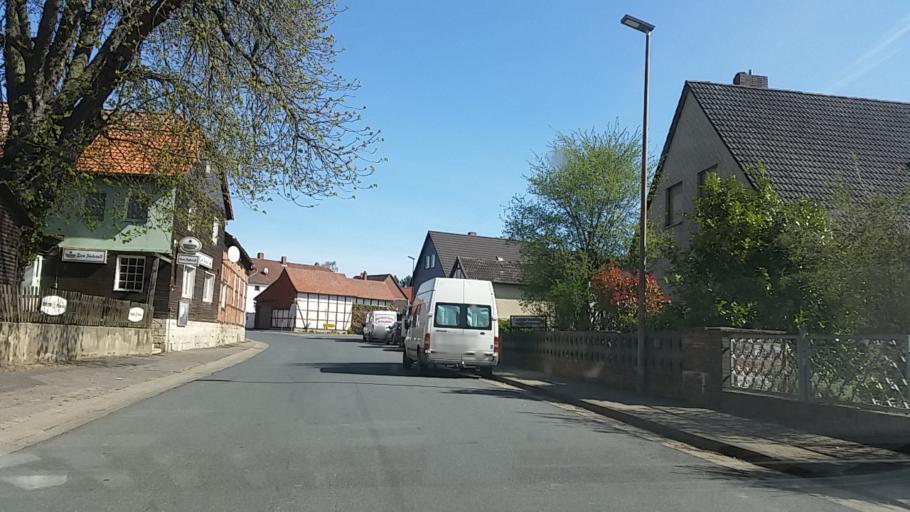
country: DE
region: Lower Saxony
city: Schoppenstedt
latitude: 52.1635
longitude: 10.7865
